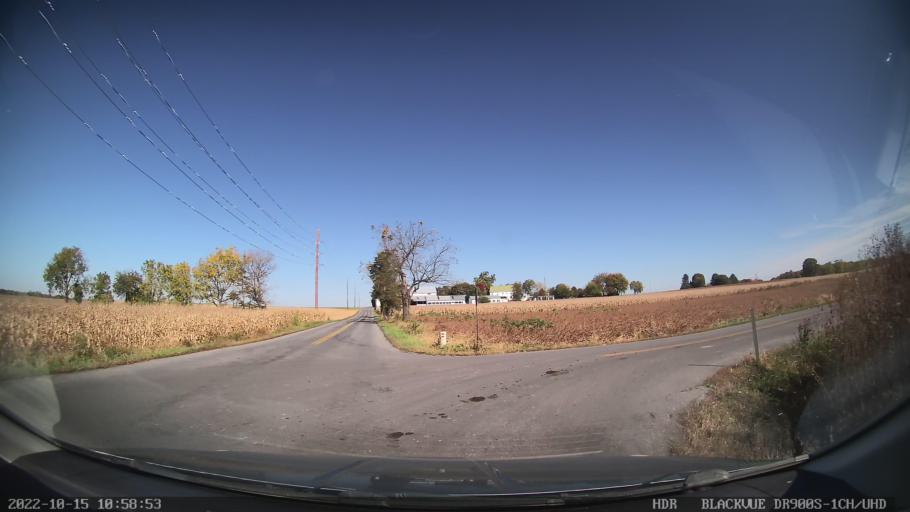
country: US
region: Pennsylvania
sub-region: Berks County
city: Kutztown
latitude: 40.5119
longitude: -75.7488
